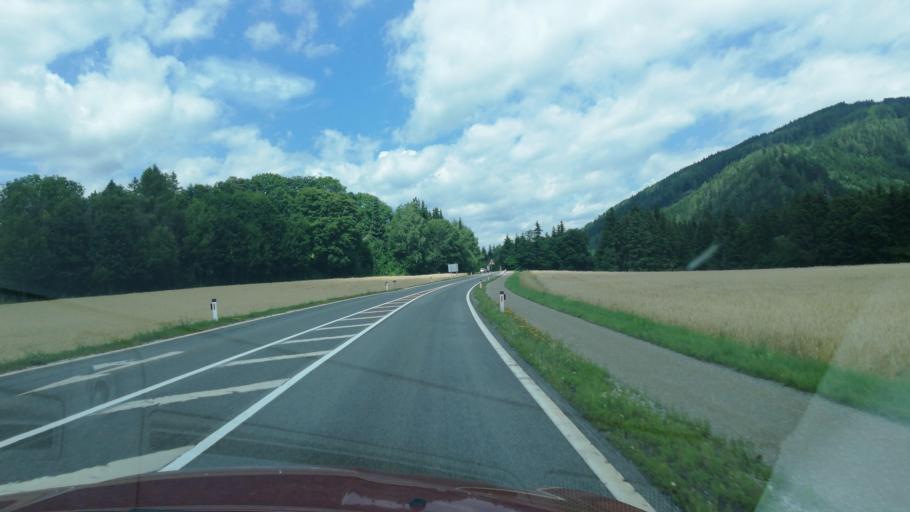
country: AT
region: Styria
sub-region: Politischer Bezirk Murtal
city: Oberkurzheim
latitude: 47.2327
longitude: 14.5485
